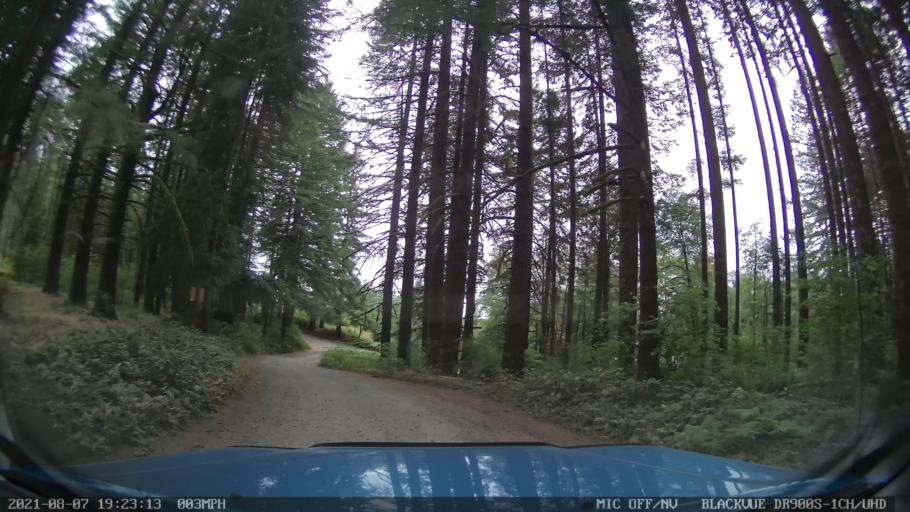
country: US
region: Oregon
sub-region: Linn County
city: Lyons
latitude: 44.8527
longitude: -122.6598
